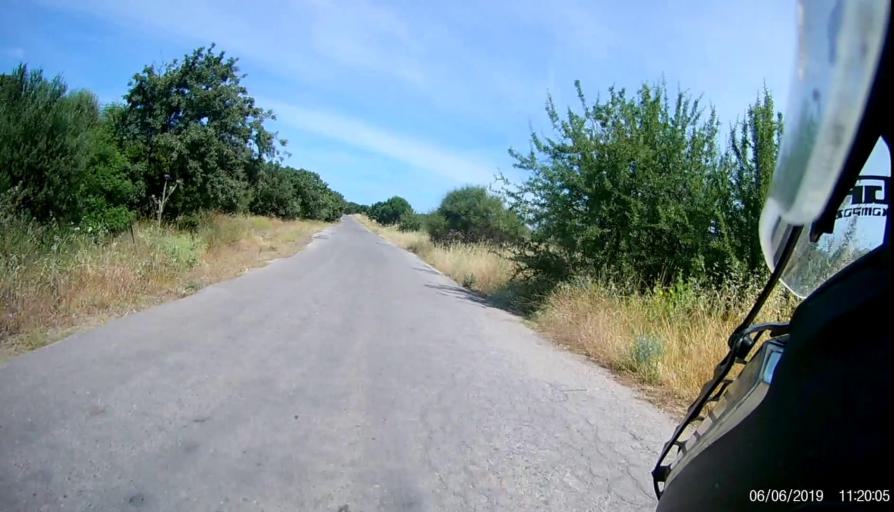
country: TR
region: Canakkale
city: Gulpinar
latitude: 39.6627
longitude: 26.1638
